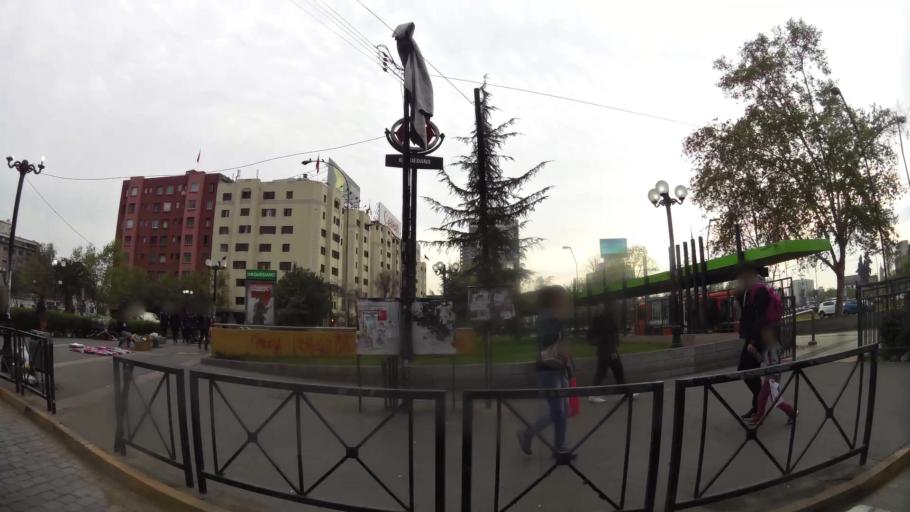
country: CL
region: Santiago Metropolitan
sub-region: Provincia de Santiago
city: Santiago
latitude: -33.4371
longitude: -70.6331
